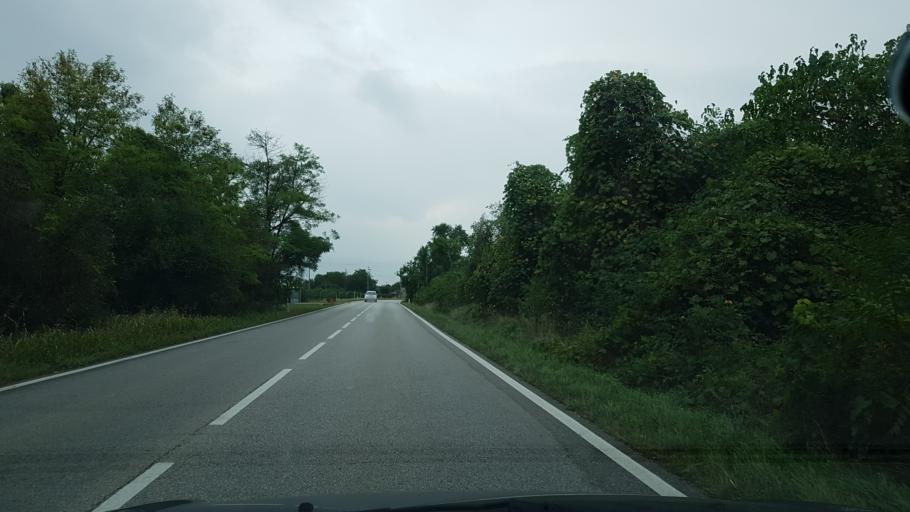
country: IT
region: Friuli Venezia Giulia
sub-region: Provincia di Udine
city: San Giovanni al Natisone
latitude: 45.9500
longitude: 13.3947
